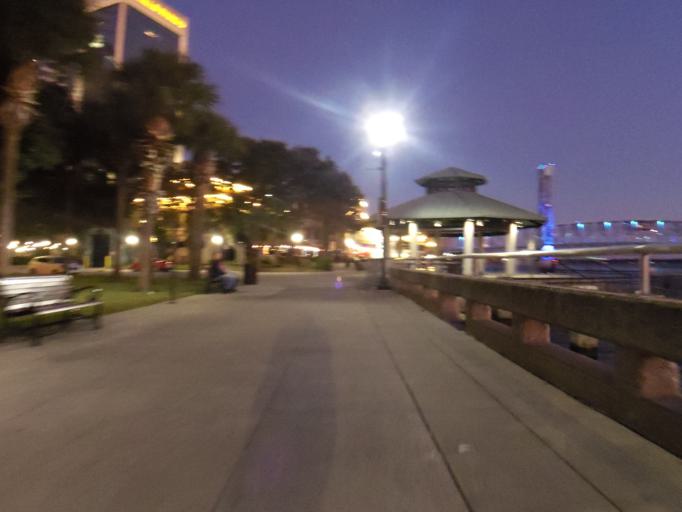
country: US
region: Florida
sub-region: Duval County
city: Jacksonville
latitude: 30.3244
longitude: -81.6618
